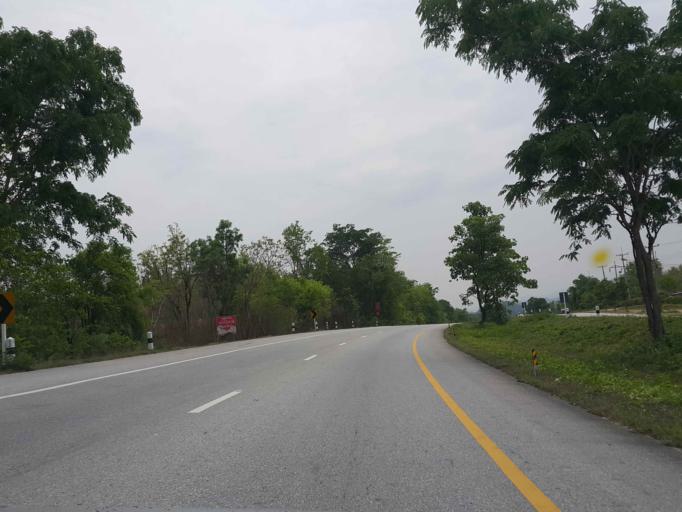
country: TH
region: Lampang
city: Sop Prap
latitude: 17.7841
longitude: 99.2598
